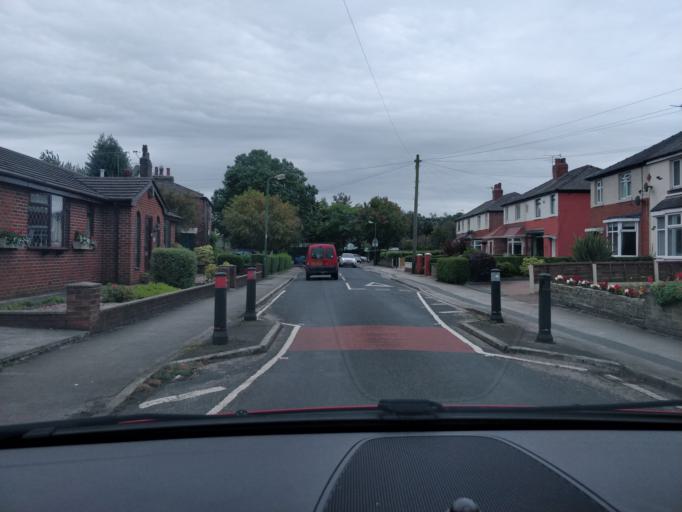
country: GB
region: England
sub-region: Lancashire
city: Ormskirk
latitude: 53.6069
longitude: -2.8414
